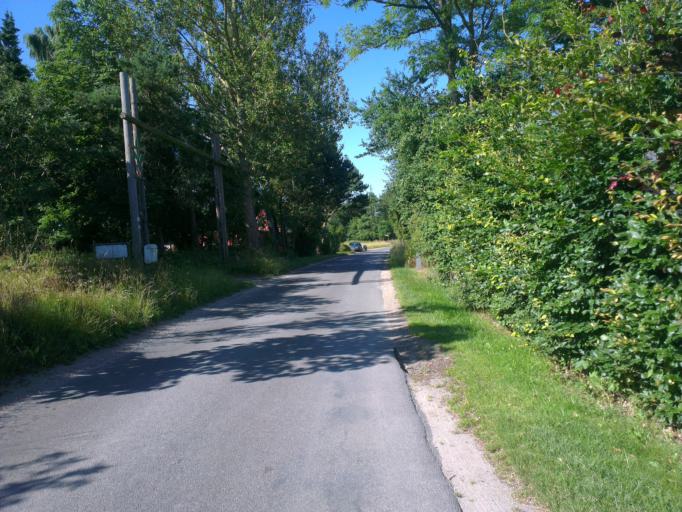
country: DK
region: Capital Region
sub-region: Frederikssund Kommune
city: Frederikssund
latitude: 55.7881
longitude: 12.0393
